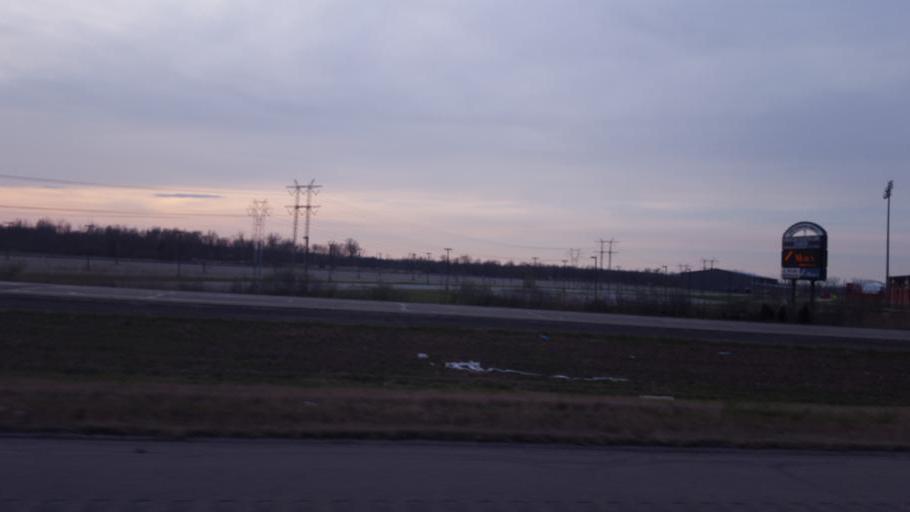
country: US
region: Ohio
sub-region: Lorain County
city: Avon
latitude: 41.4574
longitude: -82.0621
